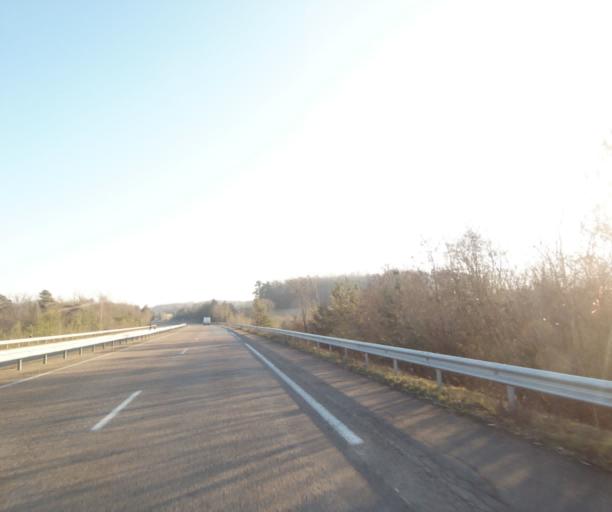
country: FR
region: Champagne-Ardenne
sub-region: Departement de la Haute-Marne
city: Chevillon
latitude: 48.5112
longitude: 5.0944
